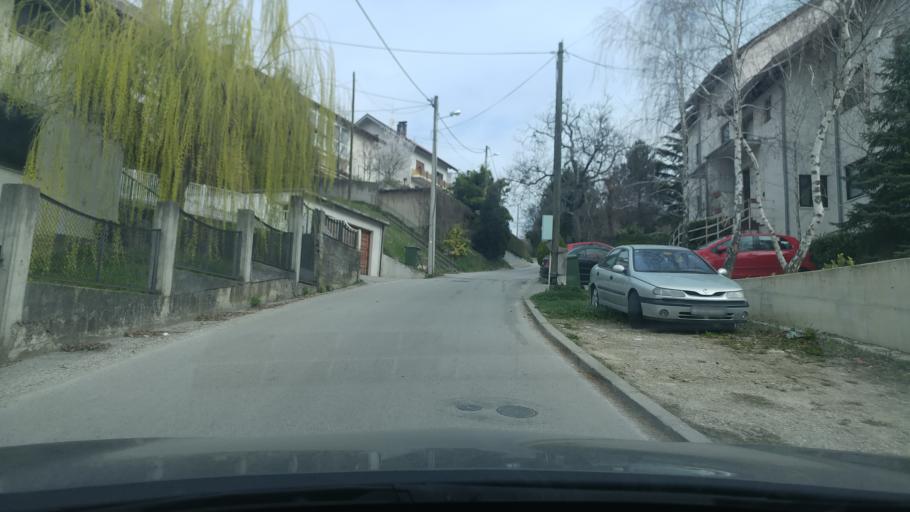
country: HR
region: Grad Zagreb
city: Stenjevec
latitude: 45.8407
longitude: 15.9242
